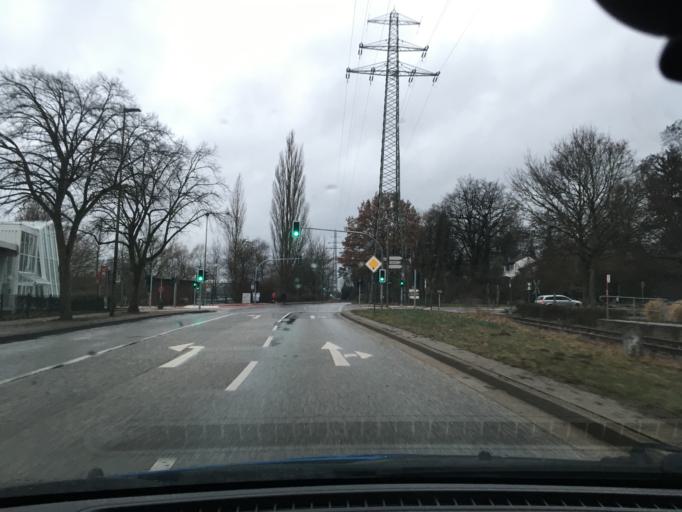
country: DE
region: Schleswig-Holstein
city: Geesthacht
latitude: 53.4279
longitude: 10.3742
